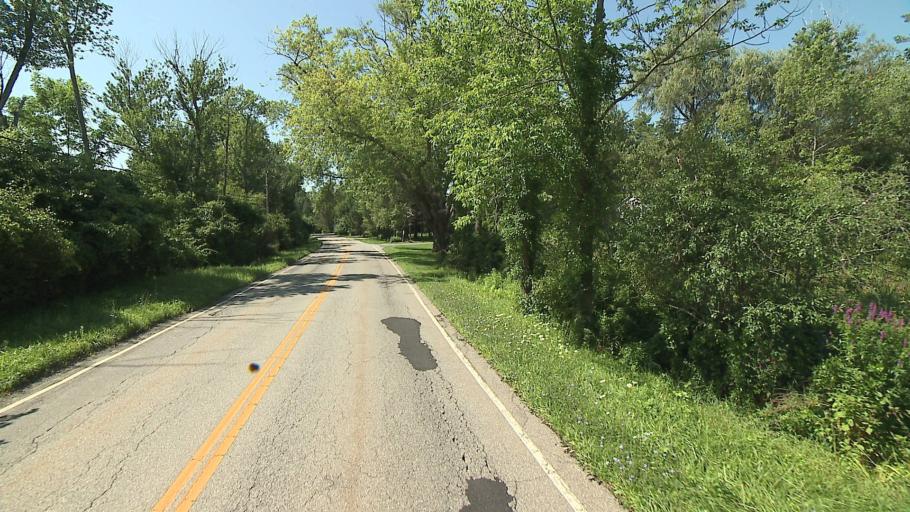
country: US
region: Connecticut
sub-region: Litchfield County
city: Kent
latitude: 41.8581
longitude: -73.4911
